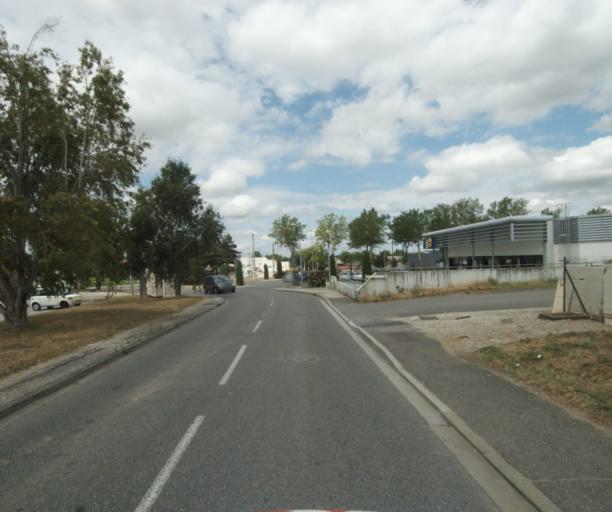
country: FR
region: Midi-Pyrenees
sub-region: Departement de la Haute-Garonne
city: Revel
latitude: 43.4538
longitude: 1.9942
